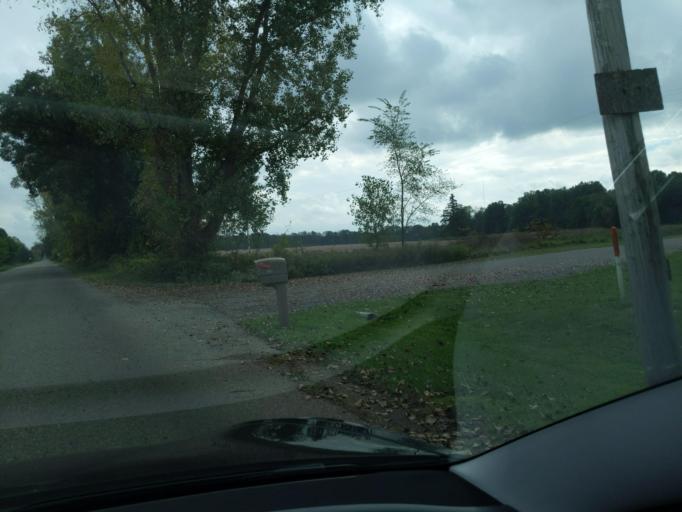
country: US
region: Michigan
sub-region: Eaton County
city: Eaton Rapids
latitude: 42.4938
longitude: -84.6557
